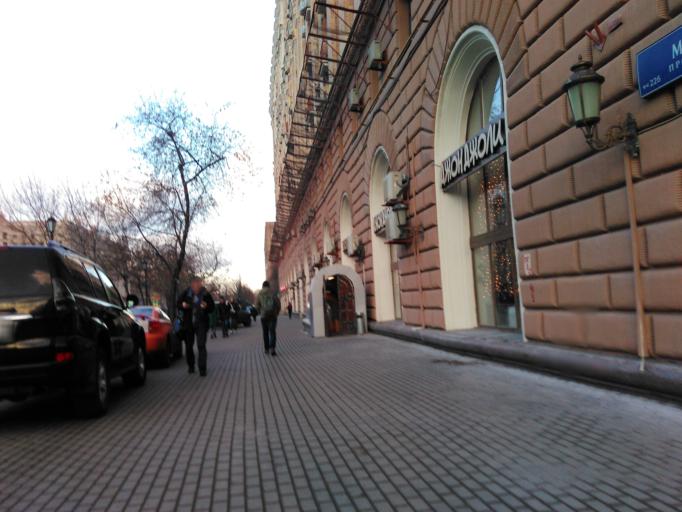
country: RU
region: Moscow
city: Mar'ina Roshcha
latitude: 55.8103
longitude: 37.6381
